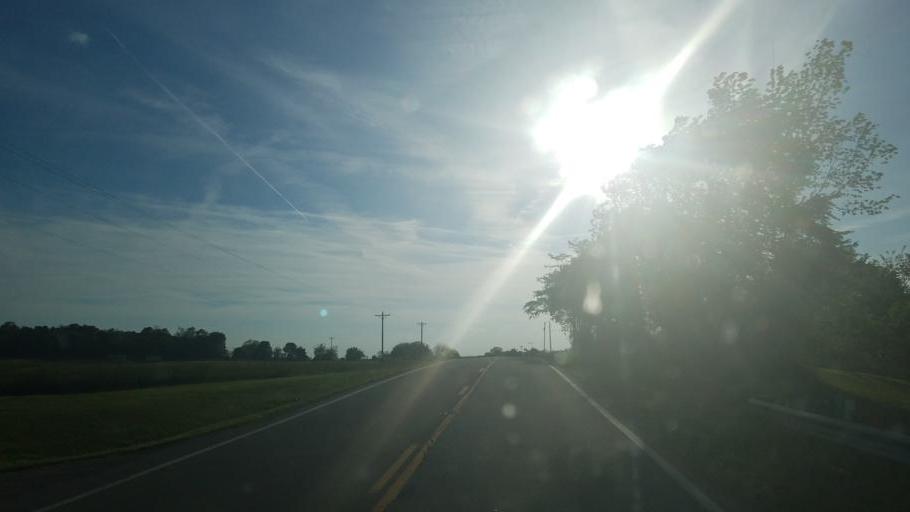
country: US
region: Ohio
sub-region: Highland County
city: Greenfield
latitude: 39.4074
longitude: -83.2933
